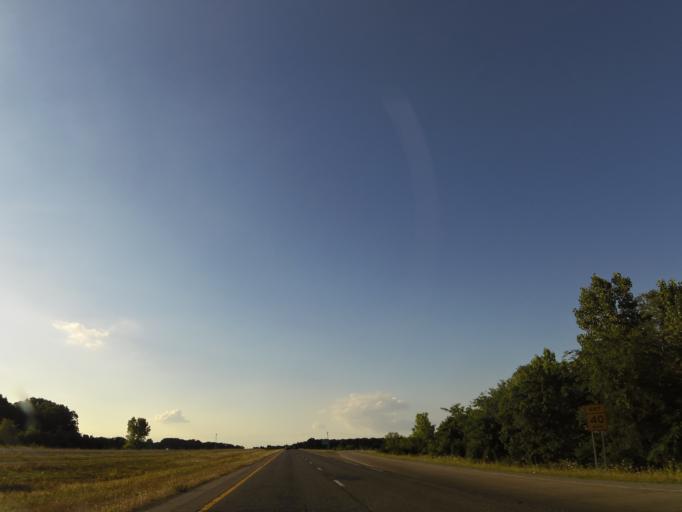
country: US
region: Tennessee
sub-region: Rutherford County
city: Smyrna
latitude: 35.9343
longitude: -86.4359
